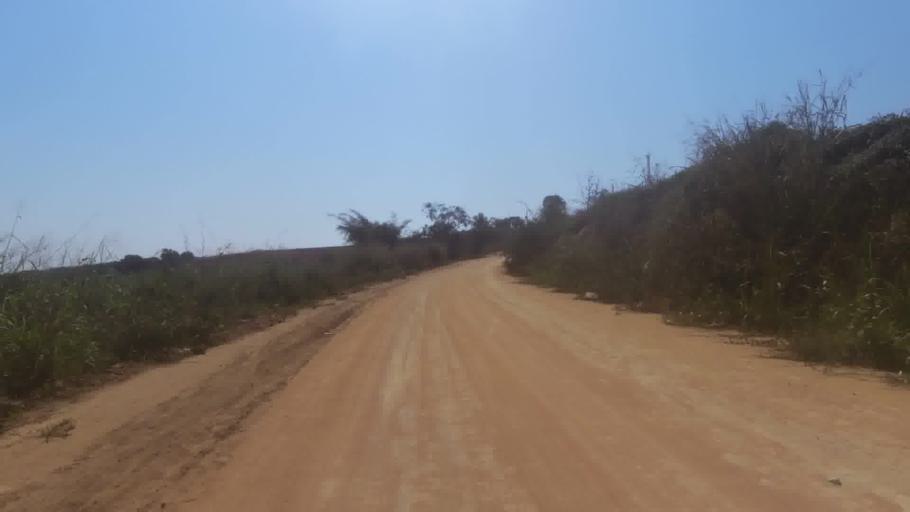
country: BR
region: Espirito Santo
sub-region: Marataizes
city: Marataizes
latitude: -21.1040
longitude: -40.8537
